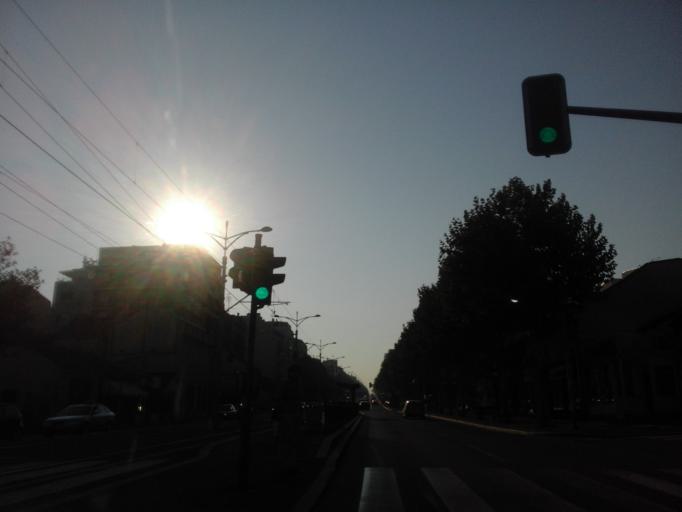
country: RS
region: Central Serbia
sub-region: Belgrade
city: Vracar
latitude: 44.8007
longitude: 20.4866
